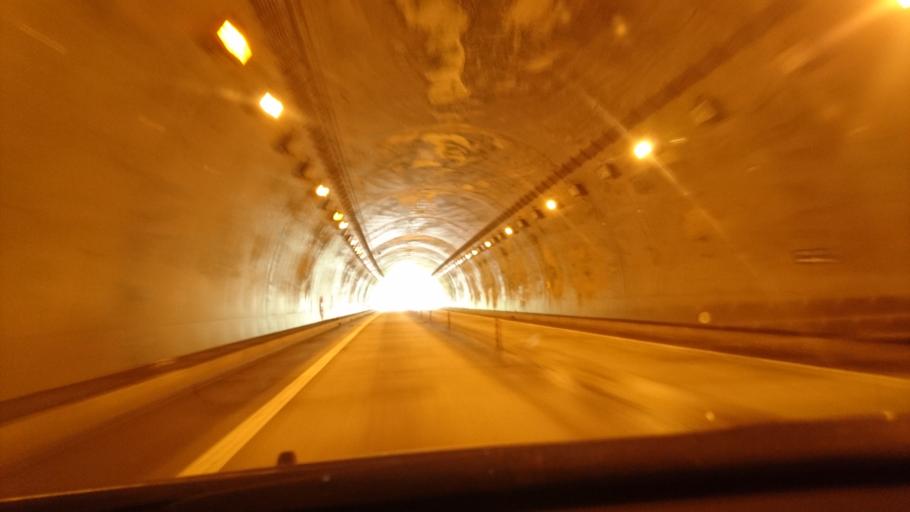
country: JP
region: Iwate
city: Ofunato
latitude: 39.0803
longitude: 141.7009
